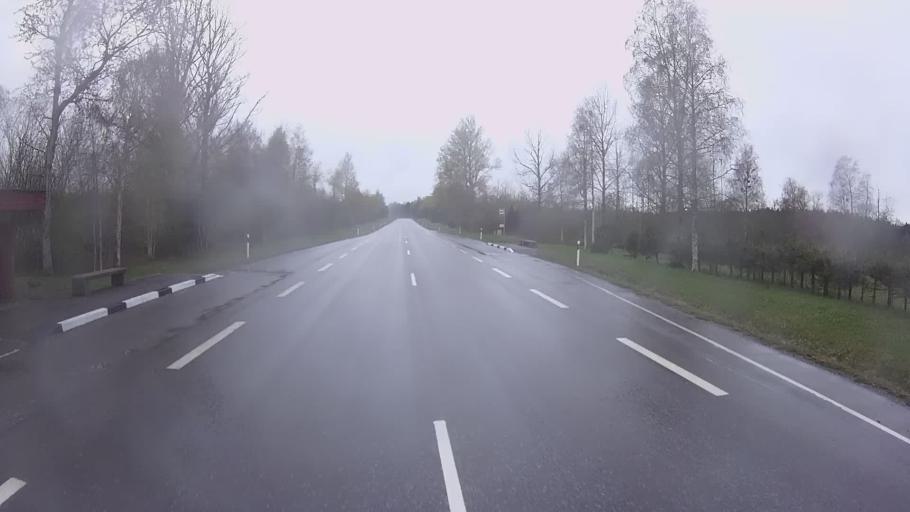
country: EE
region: Hiiumaa
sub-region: Kaerdla linn
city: Kardla
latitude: 58.9909
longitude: 22.5193
